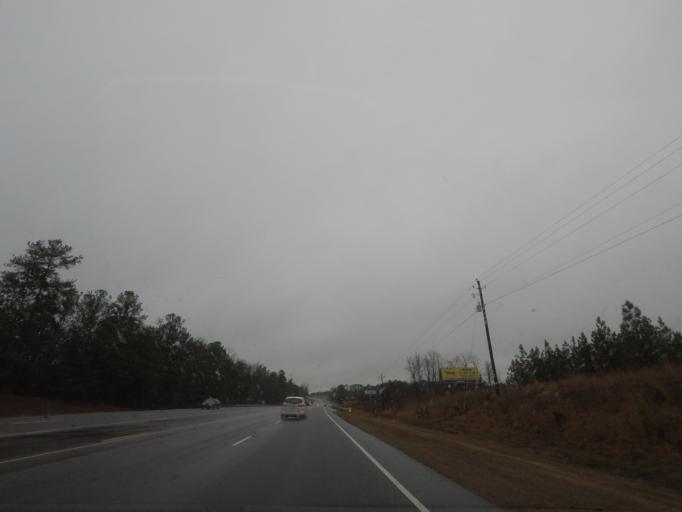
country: US
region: North Carolina
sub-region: Lee County
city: Broadway
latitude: 35.3550
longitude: -79.1093
